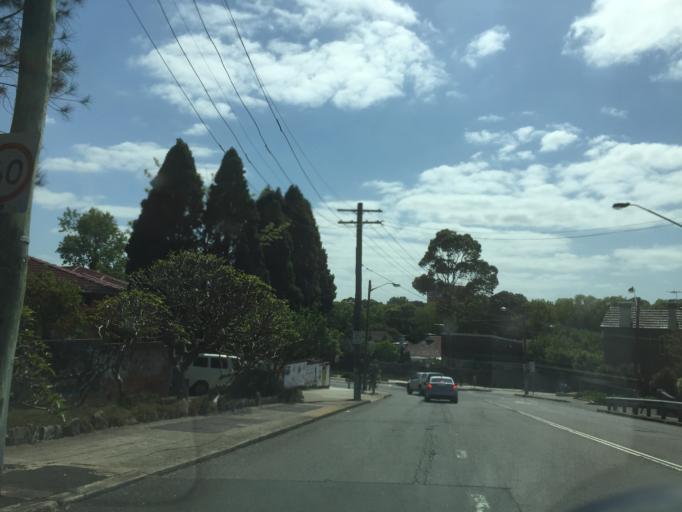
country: AU
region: New South Wales
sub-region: Marrickville
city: Lewisham
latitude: -33.8936
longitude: 151.1501
